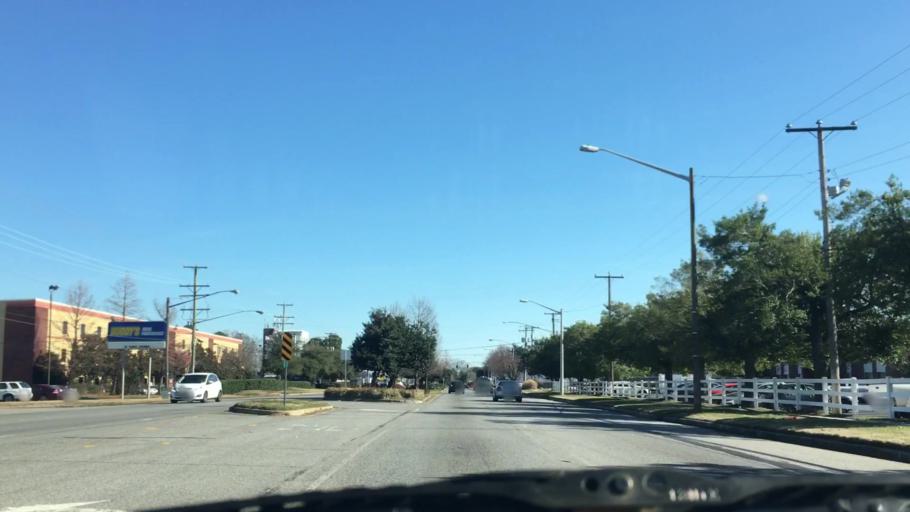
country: US
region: Virginia
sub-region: City of Norfolk
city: Norfolk
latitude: 36.9165
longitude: -76.2276
